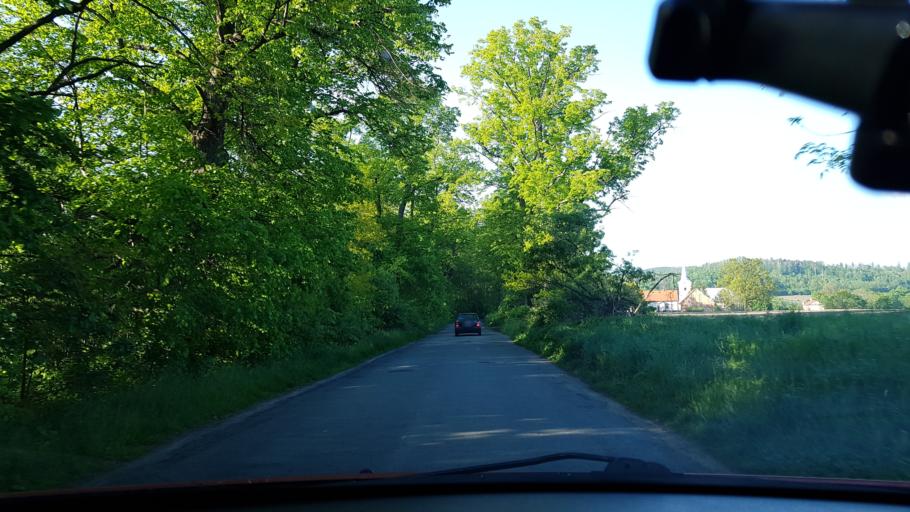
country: PL
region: Lower Silesian Voivodeship
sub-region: Powiat zabkowicki
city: Budzow
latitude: 50.6076
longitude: 16.6708
